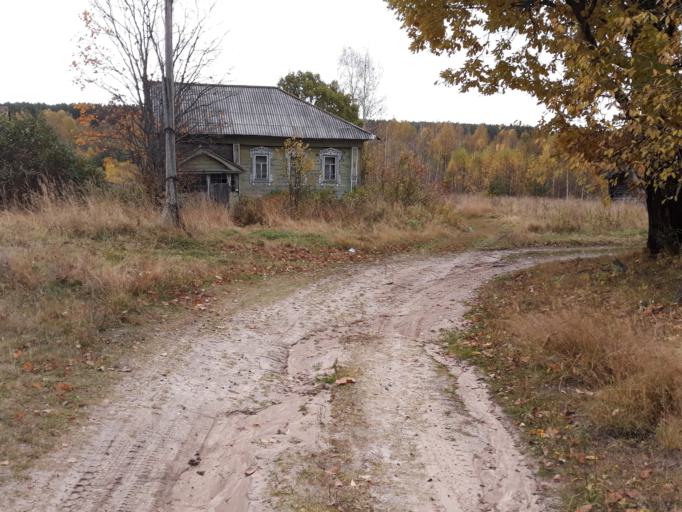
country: RU
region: Nizjnij Novgorod
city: Varnavino
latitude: 57.7140
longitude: 45.0228
